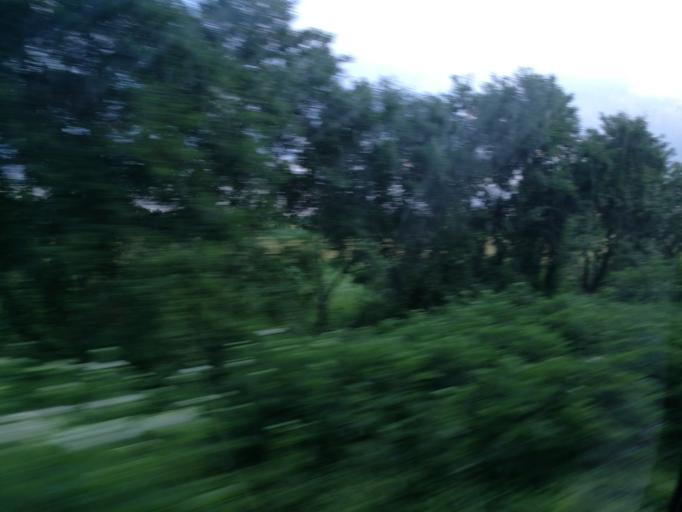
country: RO
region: Dambovita
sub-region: Comuna Titu
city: Titu
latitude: 44.6665
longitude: 25.5376
